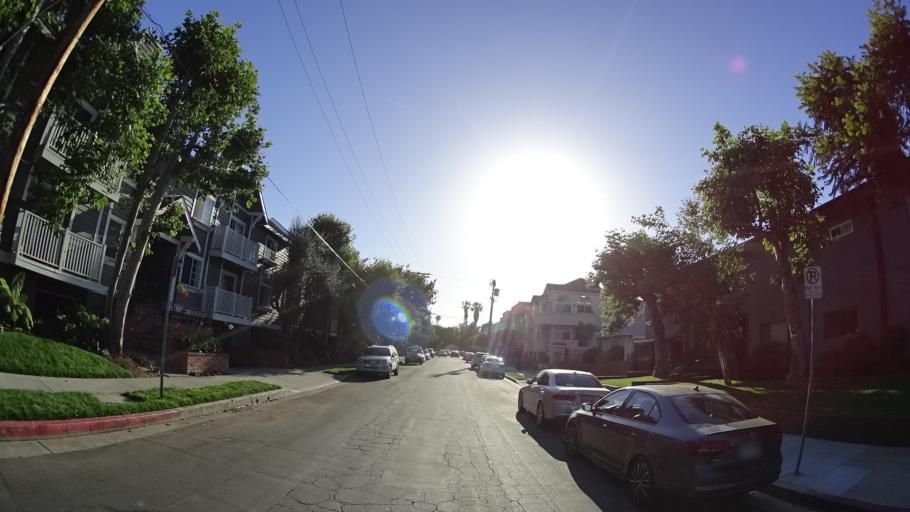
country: US
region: California
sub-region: Los Angeles County
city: North Hollywood
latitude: 34.1567
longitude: -118.3649
